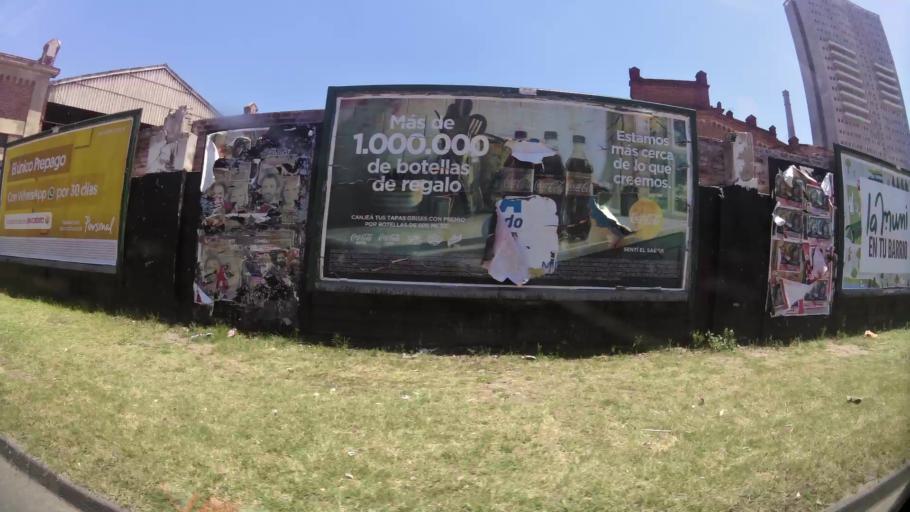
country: AR
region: Cordoba
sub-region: Departamento de Capital
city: Cordoba
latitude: -31.4022
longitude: -64.2051
